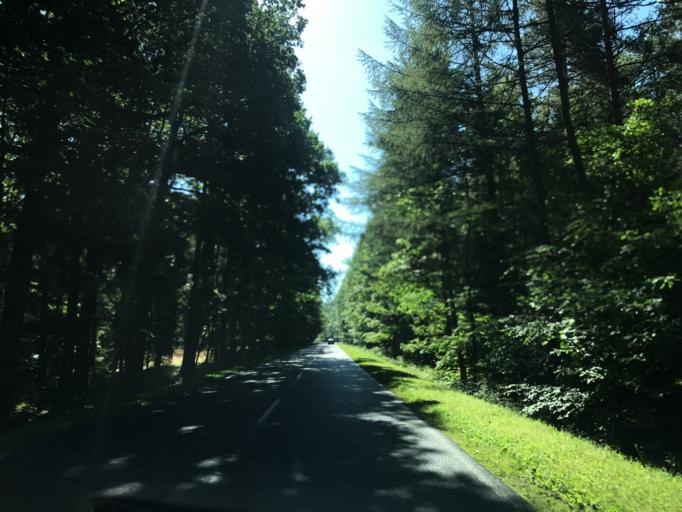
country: PL
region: Pomeranian Voivodeship
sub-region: Powiat slupski
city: Potegowo
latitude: 54.4061
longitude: 17.4478
